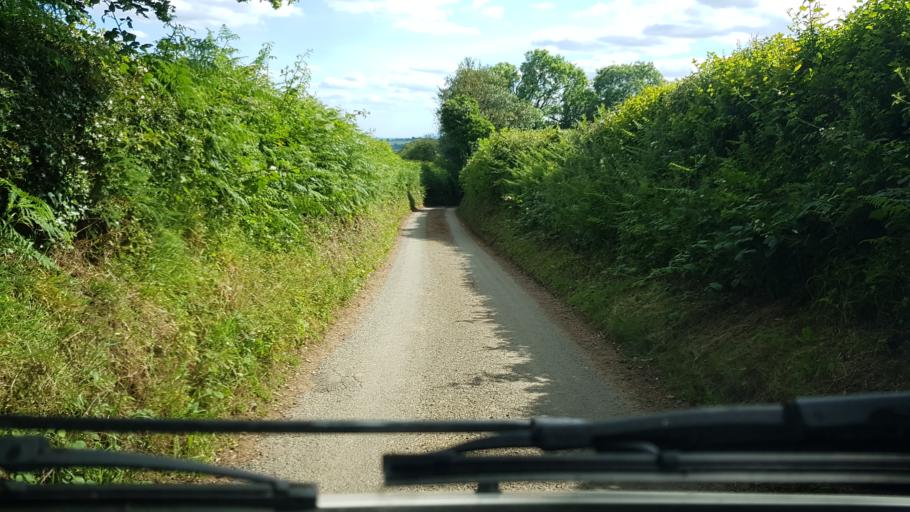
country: GB
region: England
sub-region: Shropshire
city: Romsley
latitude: 52.4604
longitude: -2.2888
